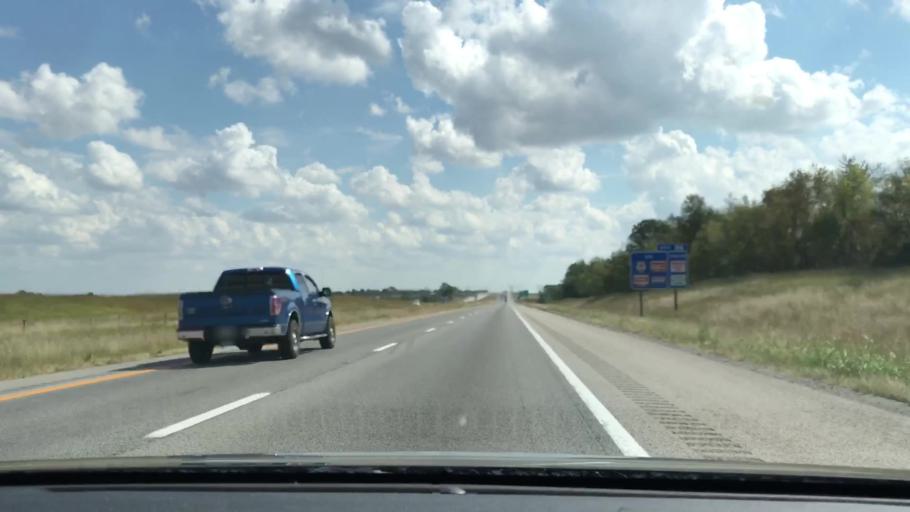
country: US
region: Kentucky
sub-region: Christian County
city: Oak Grove
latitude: 36.7074
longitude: -87.4674
